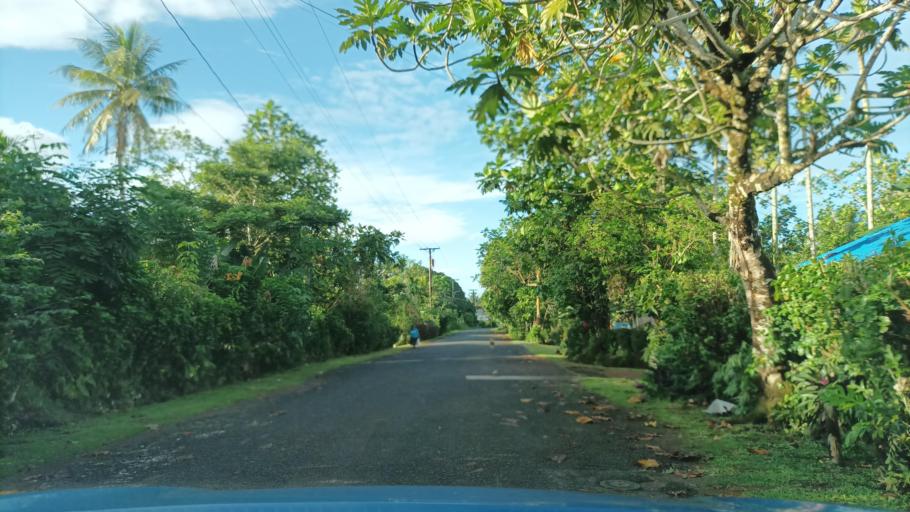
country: FM
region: Pohnpei
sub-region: Kolonia Municipality
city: Kolonia Town
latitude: 6.9640
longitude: 158.2044
